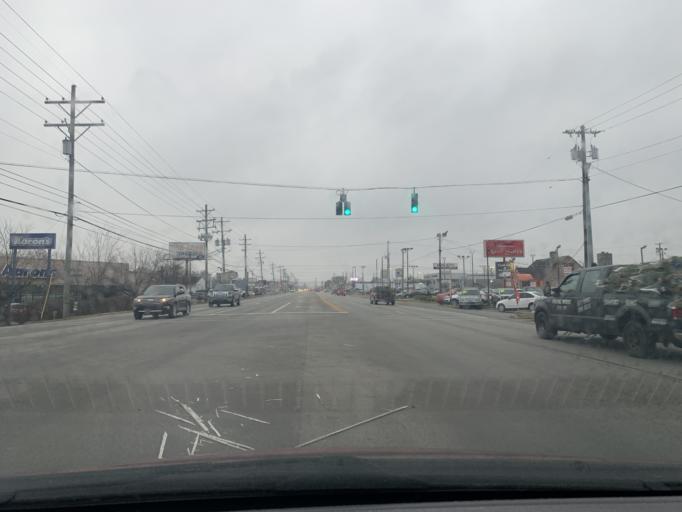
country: US
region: Kentucky
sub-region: Jefferson County
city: Okolona
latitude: 38.1610
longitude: -85.6993
